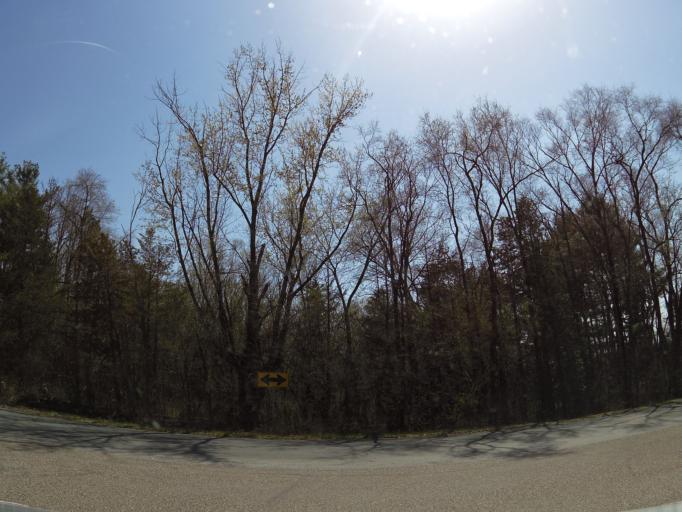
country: US
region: Wisconsin
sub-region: Saint Croix County
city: Hudson
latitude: 44.9796
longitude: -92.7058
